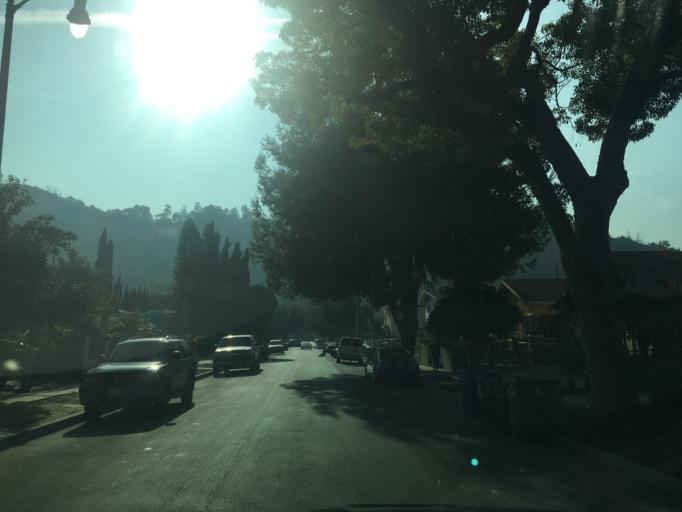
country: US
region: California
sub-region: Los Angeles County
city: Echo Park
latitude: 34.0901
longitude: -118.2332
